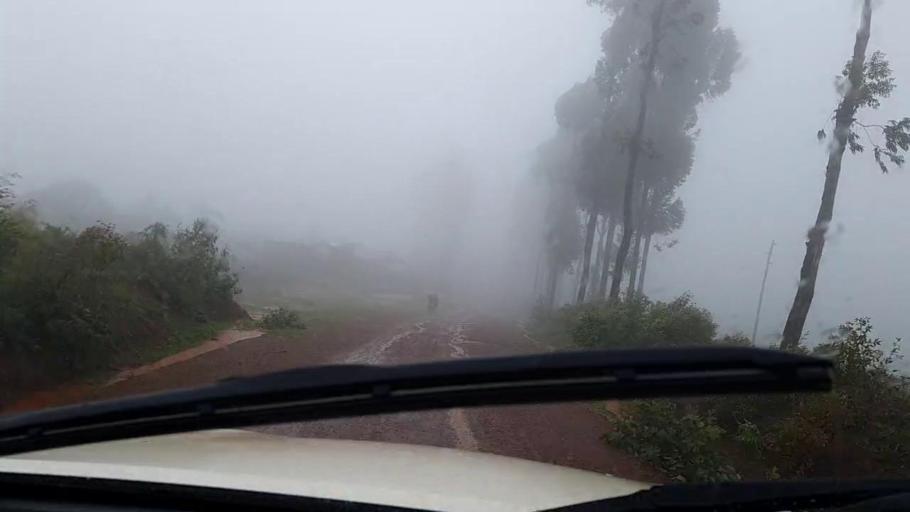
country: RW
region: Northern Province
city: Byumba
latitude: -1.7380
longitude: 30.0100
